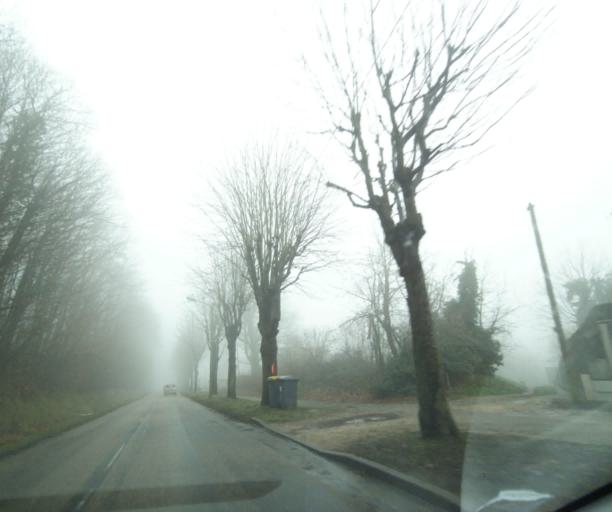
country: FR
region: Ile-de-France
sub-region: Departement de Seine-et-Marne
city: Dammartin-en-Goele
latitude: 49.0510
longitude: 2.6895
